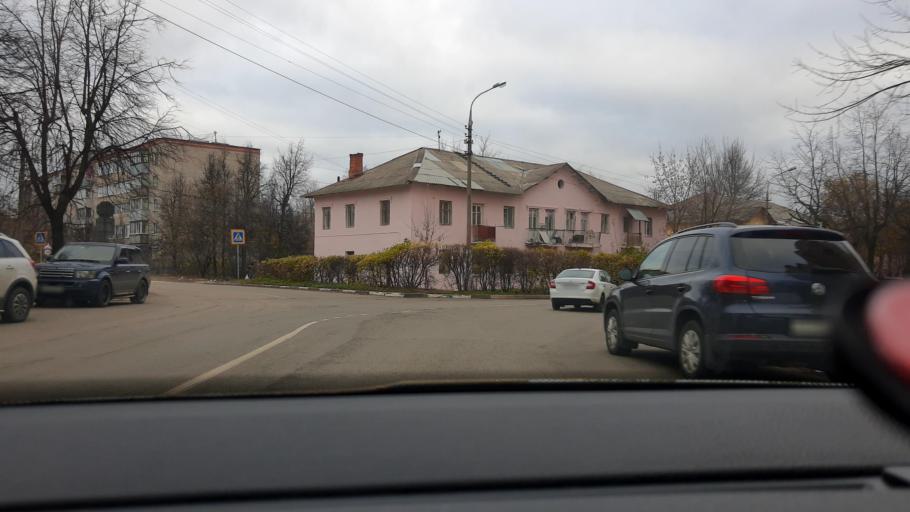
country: RU
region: Moskovskaya
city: Ivanteyevka
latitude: 55.9775
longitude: 37.9079
